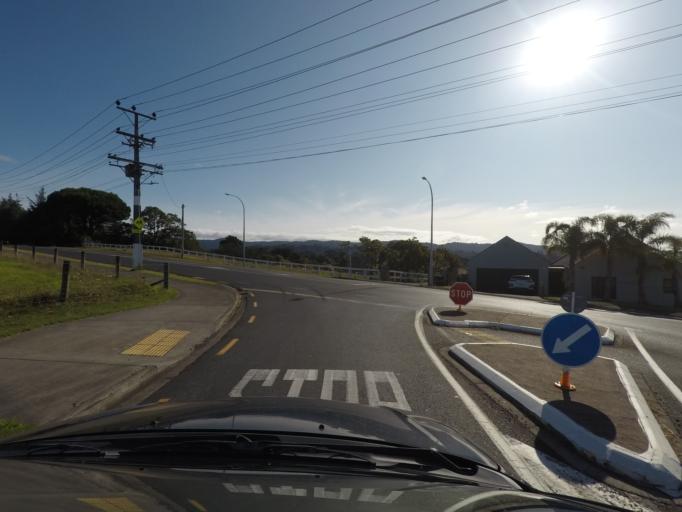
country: NZ
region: Auckland
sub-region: Auckland
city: Rosebank
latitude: -36.8748
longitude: 174.5973
